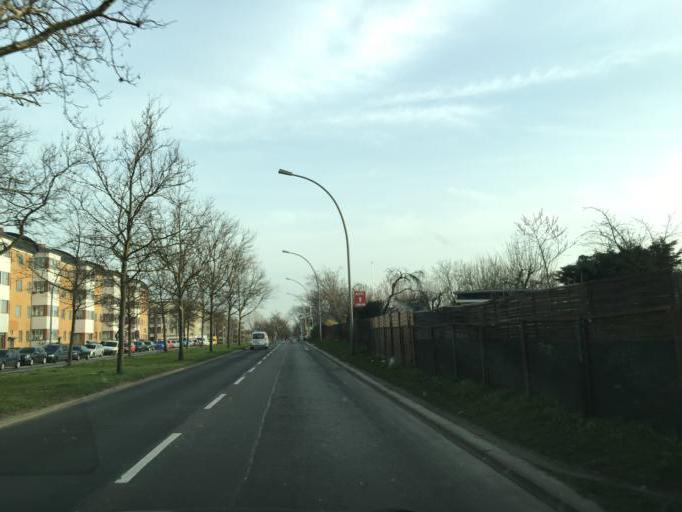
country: DE
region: Berlin
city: Heinersdorf
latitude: 52.5662
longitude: 13.4274
